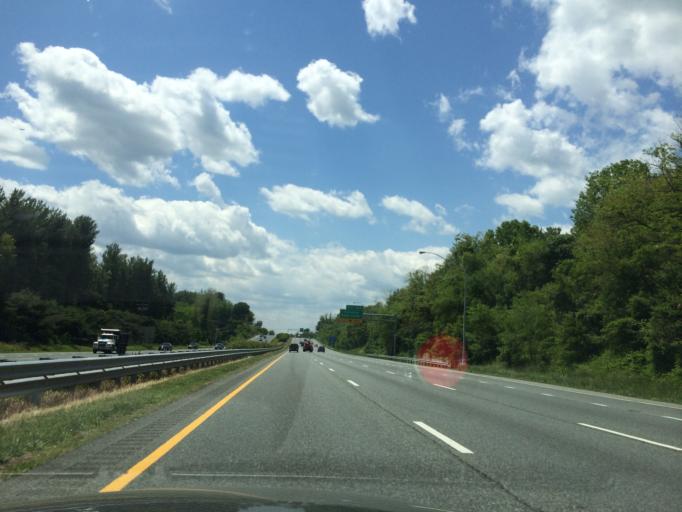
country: US
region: Maryland
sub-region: Howard County
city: Columbia
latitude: 39.2354
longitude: -76.8400
